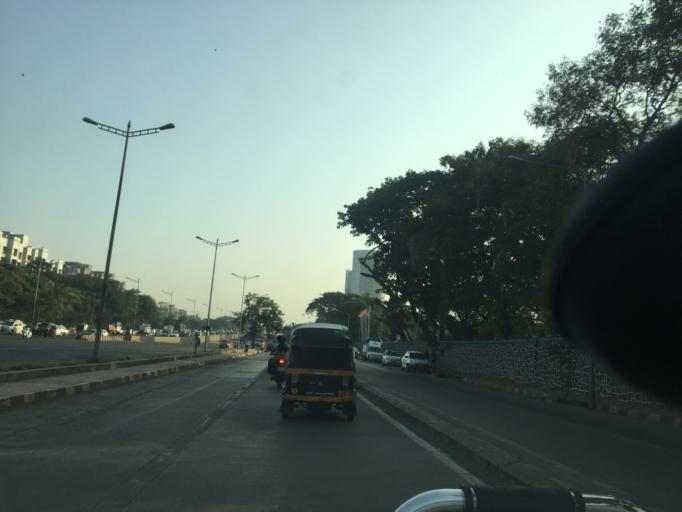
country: IN
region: Maharashtra
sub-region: Mumbai Suburban
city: Powai
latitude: 19.1493
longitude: 72.8560
